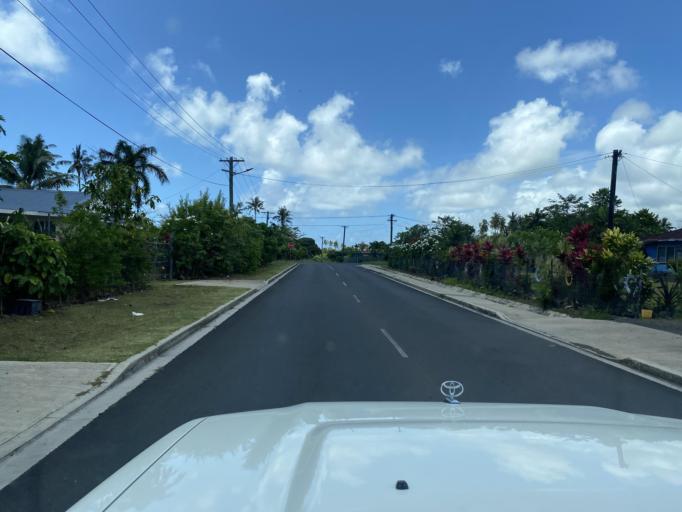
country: WS
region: Tuamasaga
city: Apia
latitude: -13.8395
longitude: -171.7577
